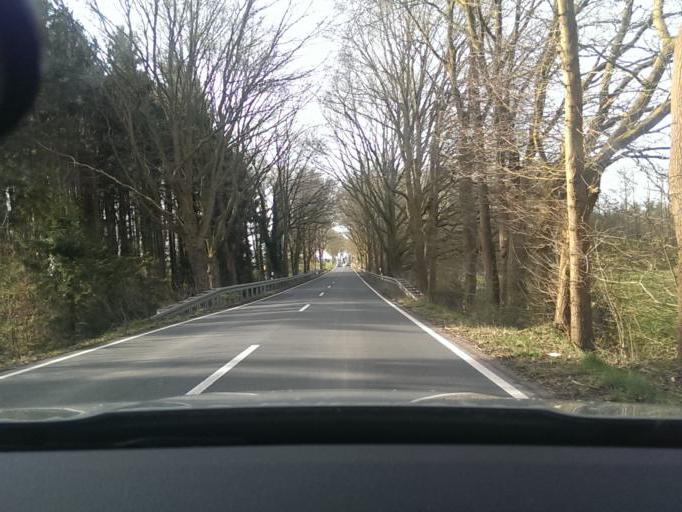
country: DE
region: Lower Saxony
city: Lindwedel
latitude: 52.5514
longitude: 9.6298
